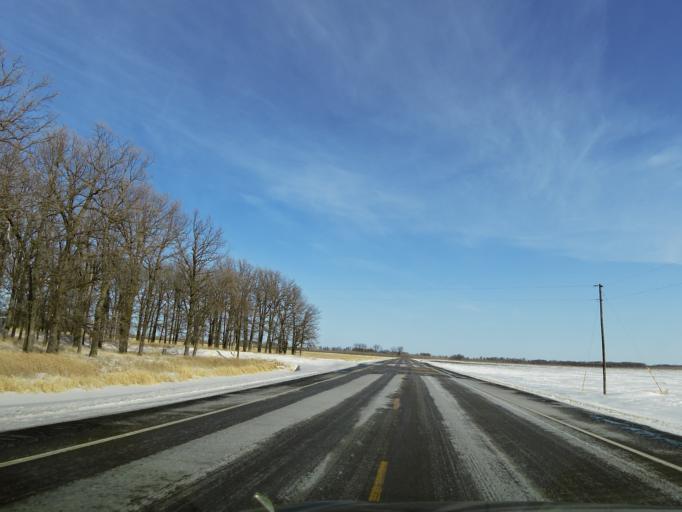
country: US
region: North Dakota
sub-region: Walsh County
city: Grafton
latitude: 48.4135
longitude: -97.1254
